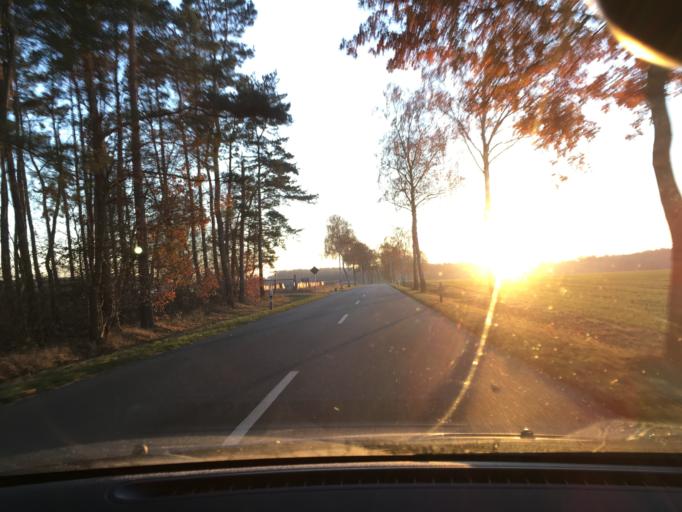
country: DE
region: Lower Saxony
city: Ebstorf
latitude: 53.0433
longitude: 10.4324
